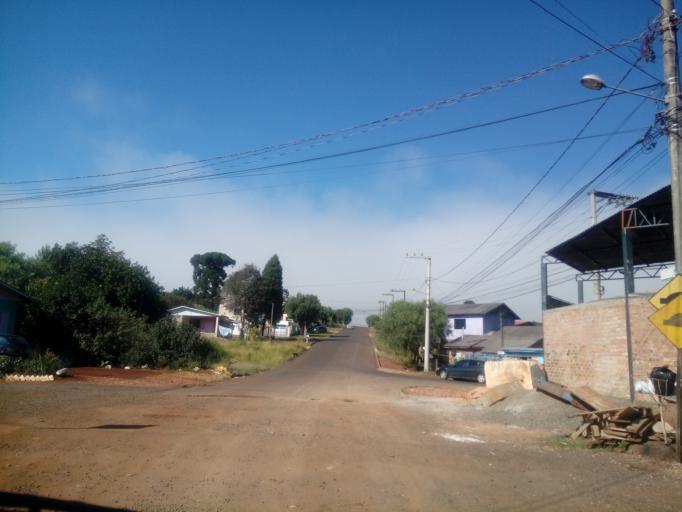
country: BR
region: Santa Catarina
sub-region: Chapeco
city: Chapeco
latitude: -27.0798
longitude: -52.6103
